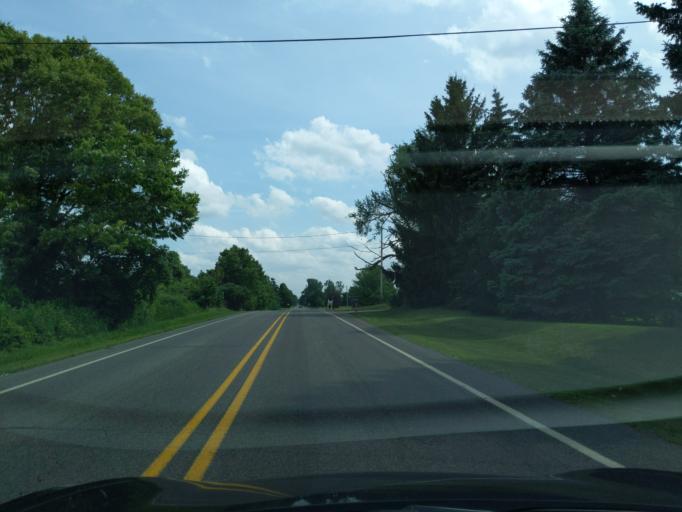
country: US
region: Michigan
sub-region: Eaton County
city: Dimondale
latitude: 42.6155
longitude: -84.6027
